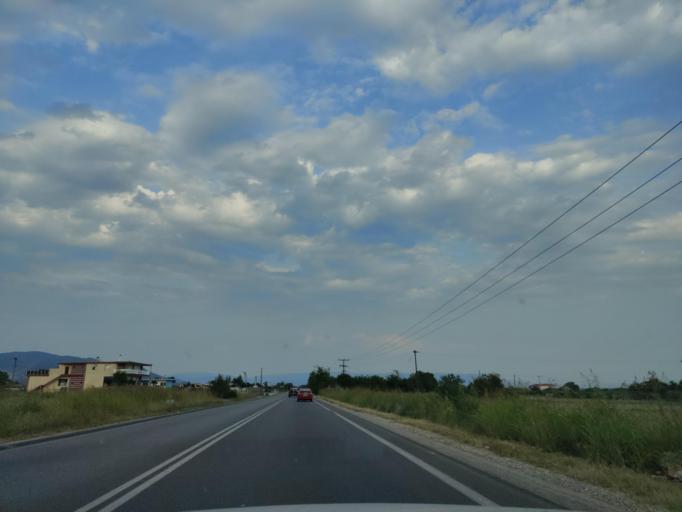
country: GR
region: East Macedonia and Thrace
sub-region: Nomos Dramas
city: Xiropotamos
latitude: 41.1596
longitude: 24.0905
